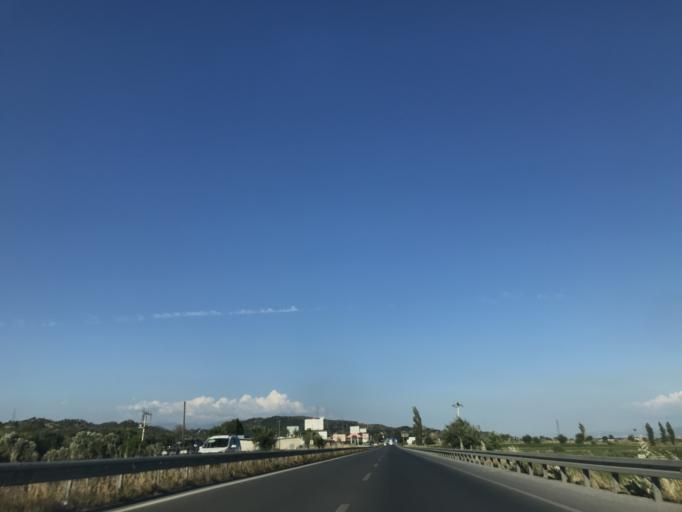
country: TR
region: Aydin
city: Ortaklar
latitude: 37.8322
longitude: 27.5126
